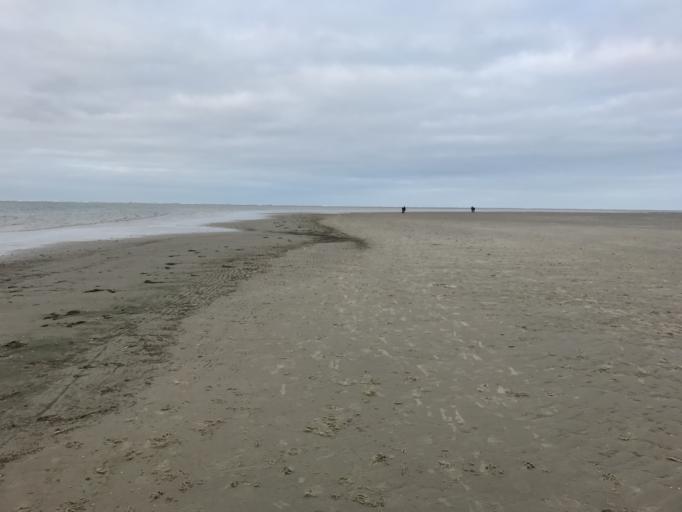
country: DE
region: Lower Saxony
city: Borkum
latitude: 53.5920
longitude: 6.6546
